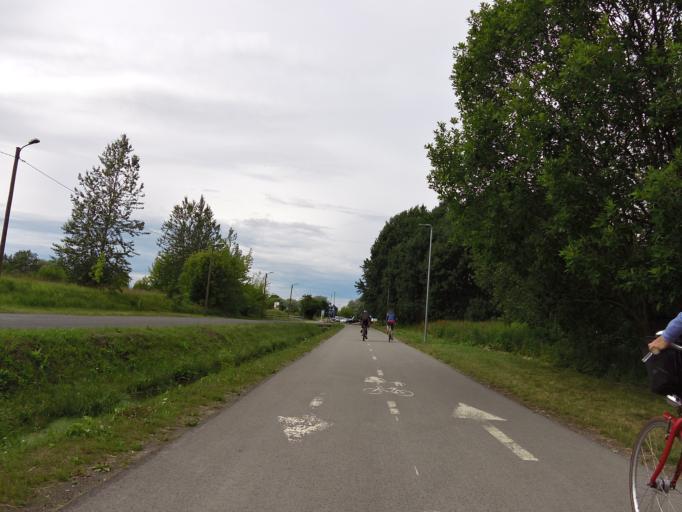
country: EE
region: Harju
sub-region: Tallinna linn
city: Tallinn
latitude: 59.4337
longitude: 24.6850
